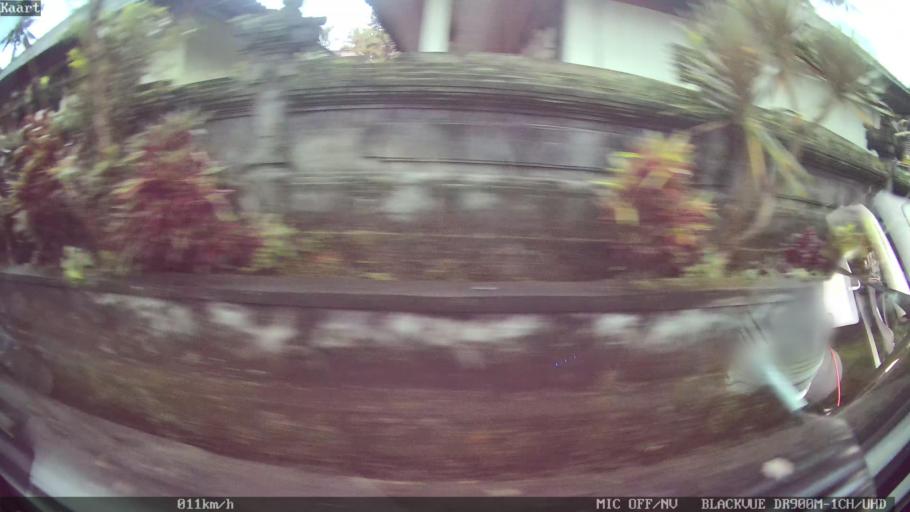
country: ID
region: Bali
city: Pegongan
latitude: -8.4885
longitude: 115.2386
